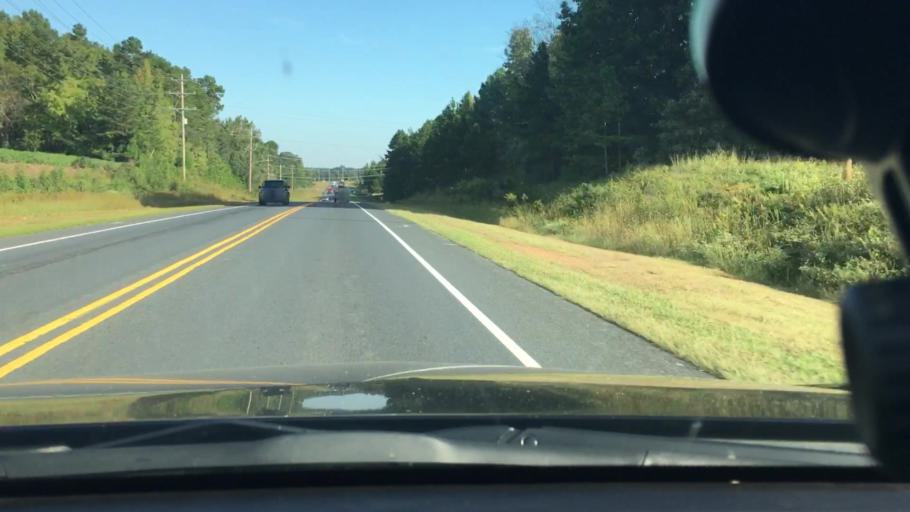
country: US
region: North Carolina
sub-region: Stanly County
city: Albemarle
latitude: 35.3699
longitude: -80.1700
